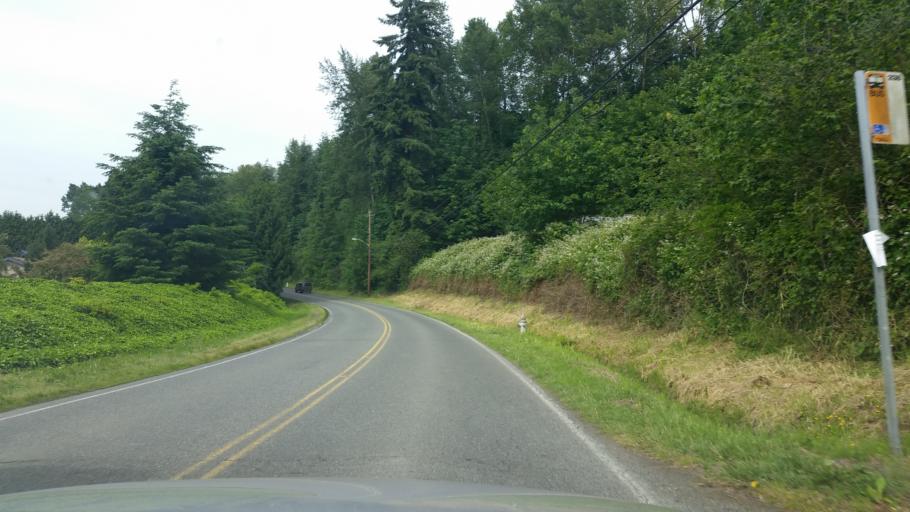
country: US
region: Washington
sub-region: King County
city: Bothell
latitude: 47.7531
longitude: -122.1885
